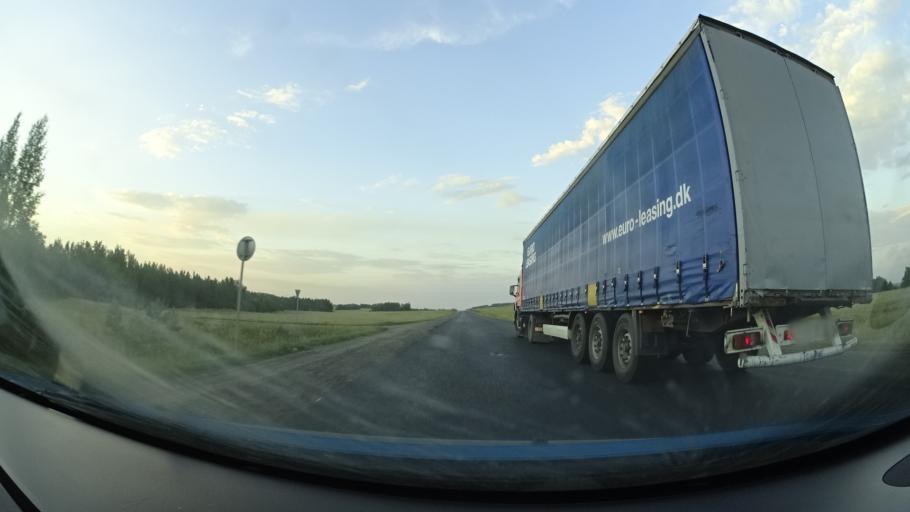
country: RU
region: Orenburg
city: Severnoye
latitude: 54.1543
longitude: 52.6221
